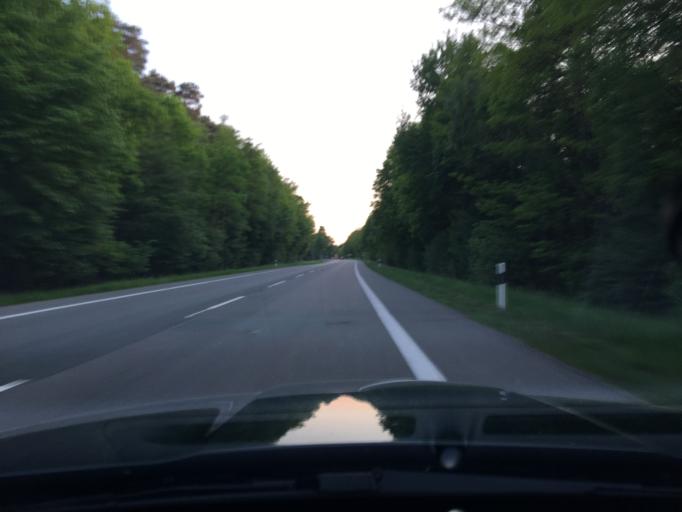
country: DE
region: North Rhine-Westphalia
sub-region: Regierungsbezirk Munster
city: Ladbergen
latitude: 52.1476
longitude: 7.7672
